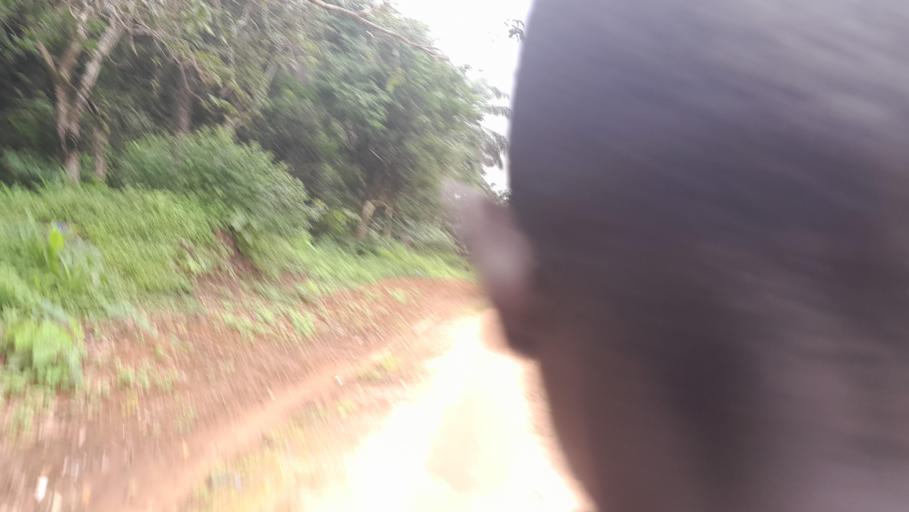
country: GN
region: Boke
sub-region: Boffa
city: Boffa
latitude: 10.0826
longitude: -13.8647
